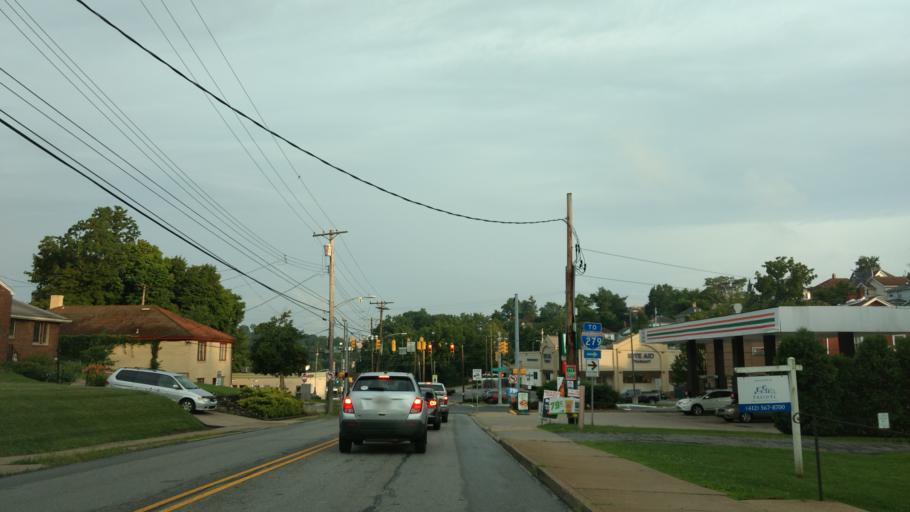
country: US
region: Pennsylvania
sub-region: Allegheny County
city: West View
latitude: 40.5230
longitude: -80.0347
